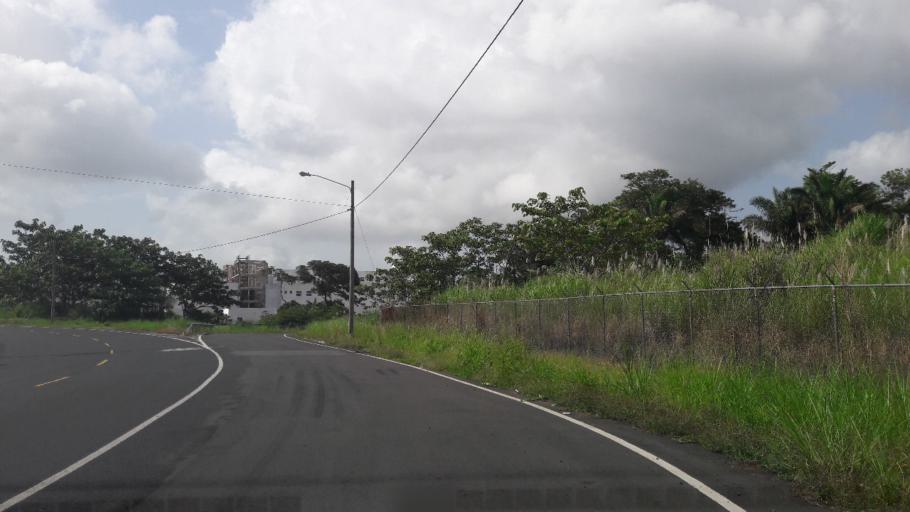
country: PA
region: Colon
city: Cativa
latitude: 9.3544
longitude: -79.8626
